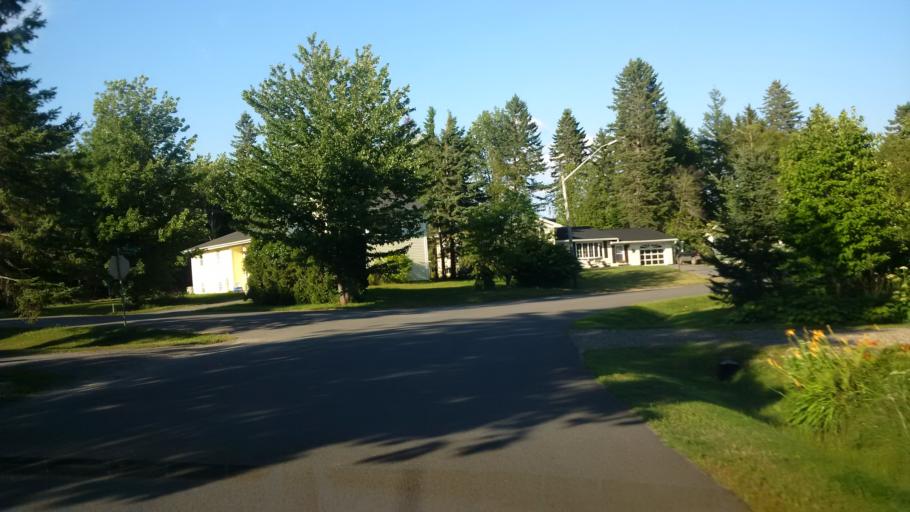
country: CA
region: New Brunswick
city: Fredericton
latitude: 45.8933
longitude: -66.6901
